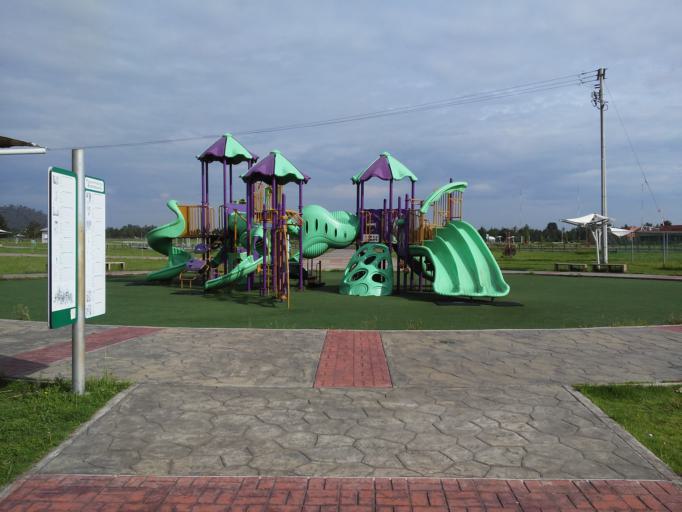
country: MX
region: Morelos
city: San Miguel Totocuitlapilco
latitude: 19.2455
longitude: -99.5850
